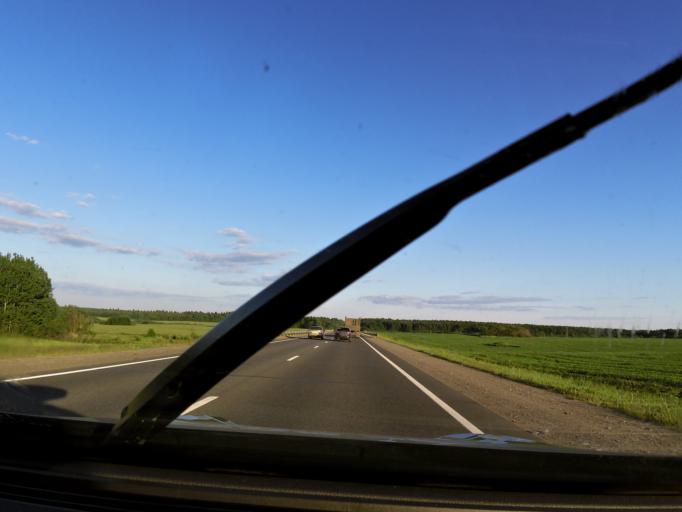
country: RU
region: Vologda
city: Vologda
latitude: 59.1441
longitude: 39.9446
